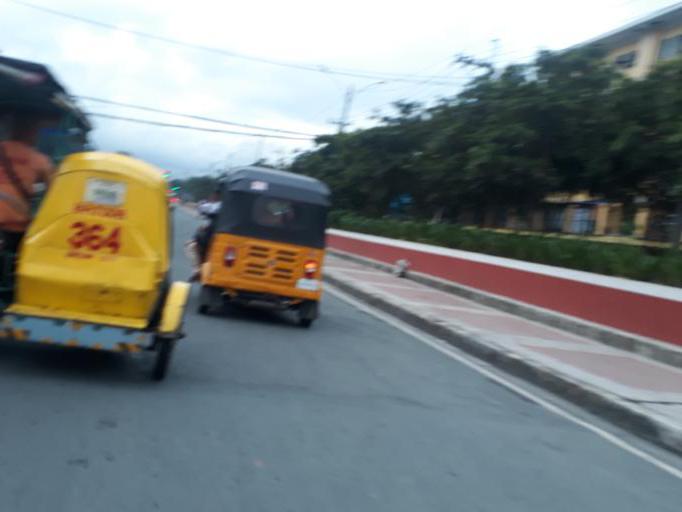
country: PH
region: Calabarzon
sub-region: Province of Rizal
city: San Mateo
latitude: 14.6897
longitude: 121.0944
